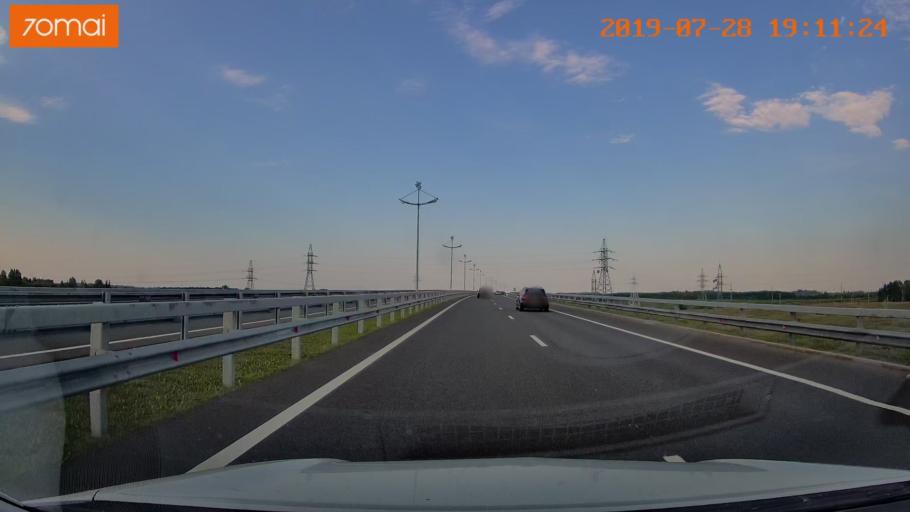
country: RU
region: Kaliningrad
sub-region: Gorod Kaliningrad
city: Pionerskiy
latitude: 54.9140
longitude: 20.2293
